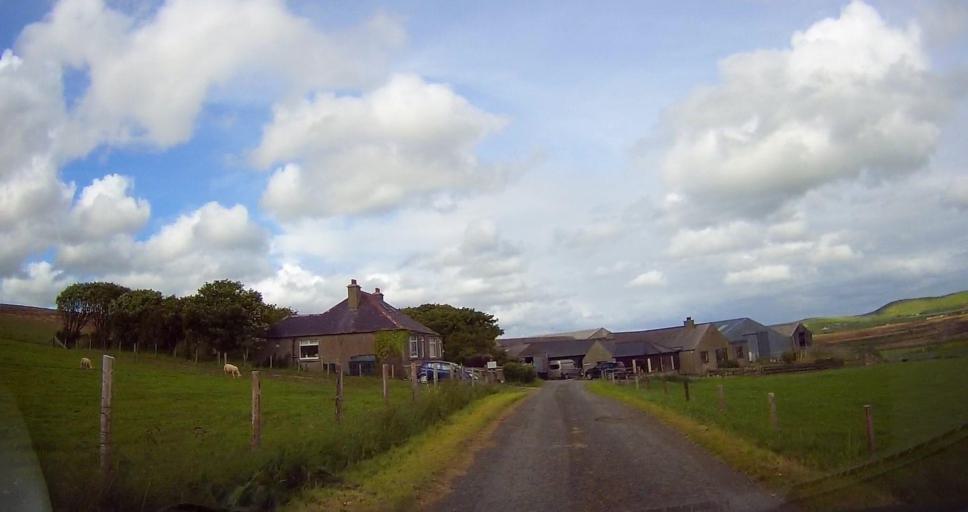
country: GB
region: Scotland
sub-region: Orkney Islands
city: Orkney
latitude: 59.0569
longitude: -3.1009
